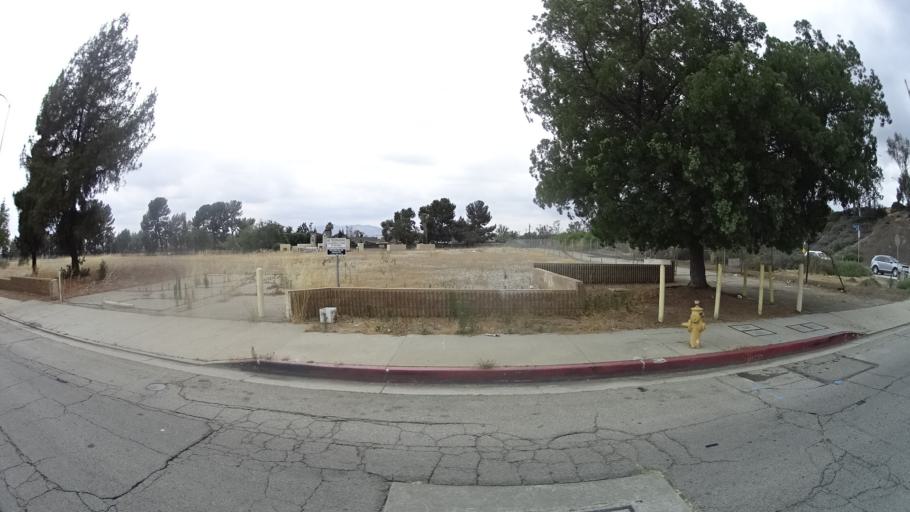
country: US
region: California
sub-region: Los Angeles County
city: San Fernando
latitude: 34.2623
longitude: -118.4420
